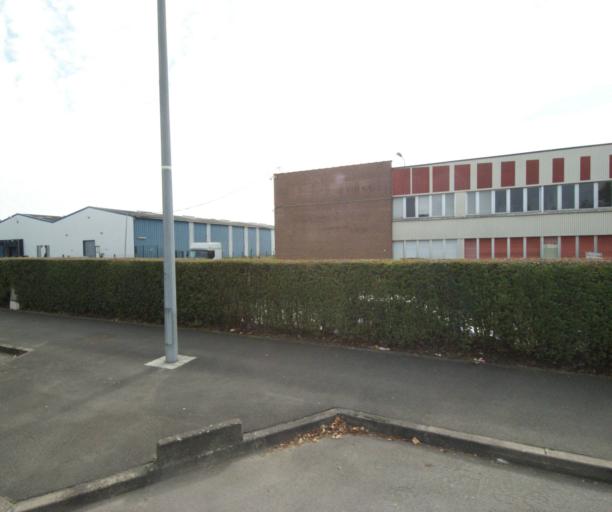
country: FR
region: Nord-Pas-de-Calais
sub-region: Departement du Nord
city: Seclin
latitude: 50.5663
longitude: 3.0354
